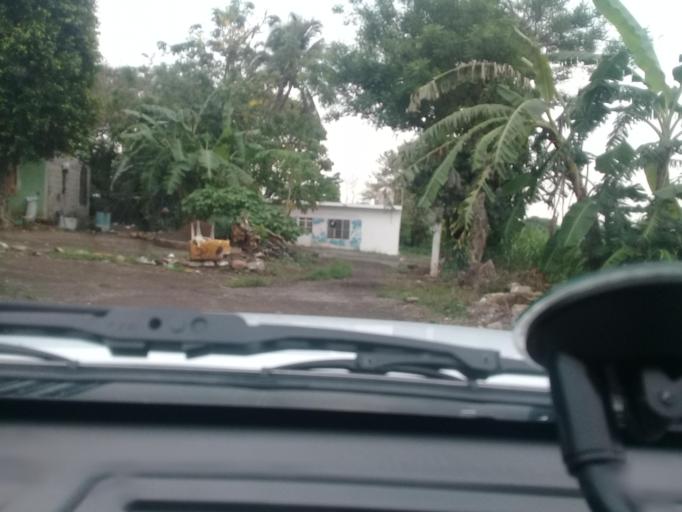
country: MX
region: Veracruz
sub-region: Puente Nacional
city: Chichicaxtle
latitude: 19.3690
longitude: -96.4333
